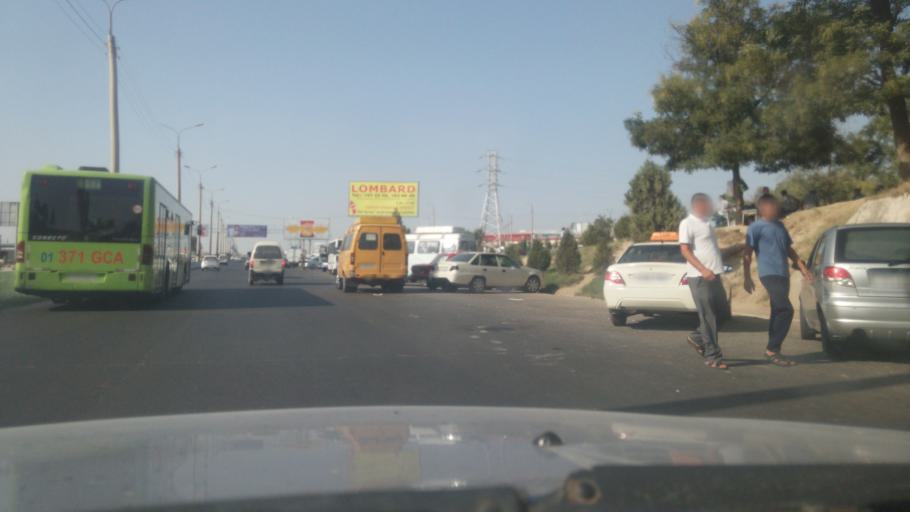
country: UZ
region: Toshkent Shahri
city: Tashkent
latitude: 41.2392
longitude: 69.1676
